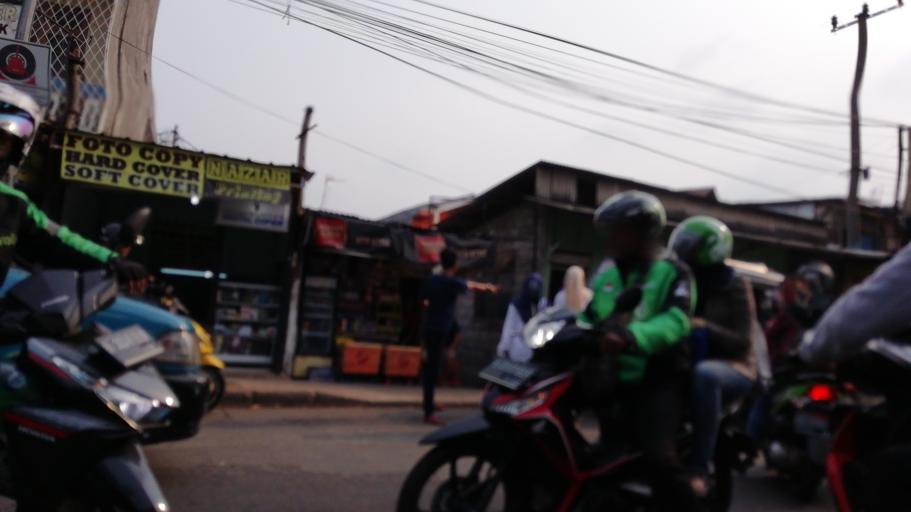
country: ID
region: West Java
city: Depok
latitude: -6.3549
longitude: 106.8416
